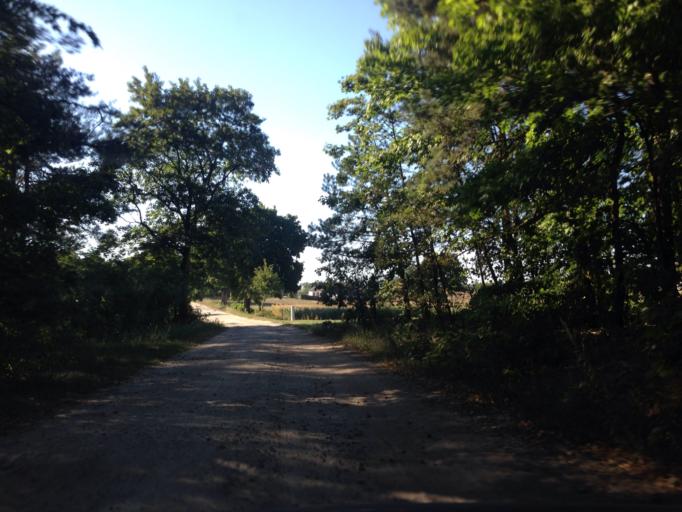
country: PL
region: Kujawsko-Pomorskie
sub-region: Powiat brodnicki
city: Gorzno
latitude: 53.1813
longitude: 19.6480
